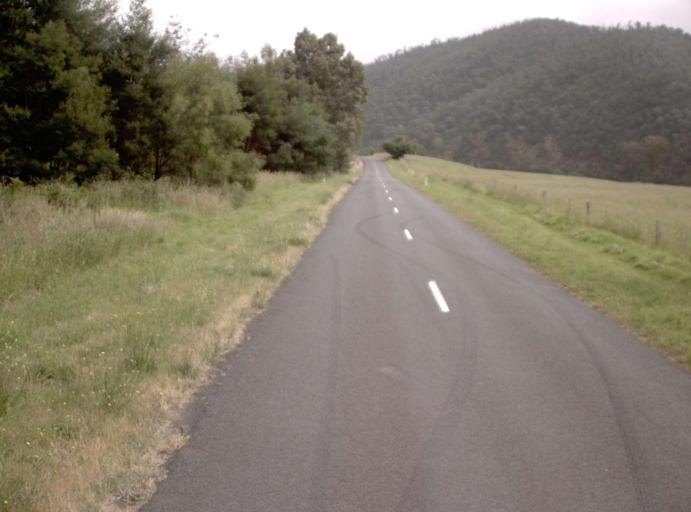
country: AU
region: Victoria
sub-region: Wellington
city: Heyfield
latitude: -37.7685
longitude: 146.6673
